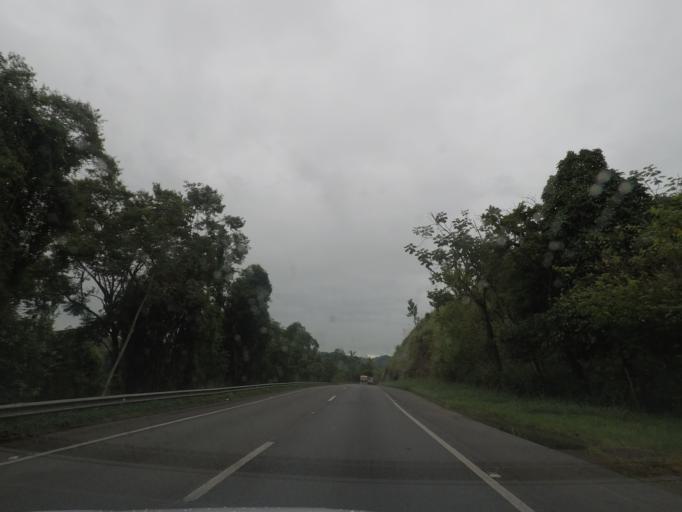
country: BR
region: Sao Paulo
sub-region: Cajati
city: Cajati
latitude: -24.7935
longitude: -48.2076
